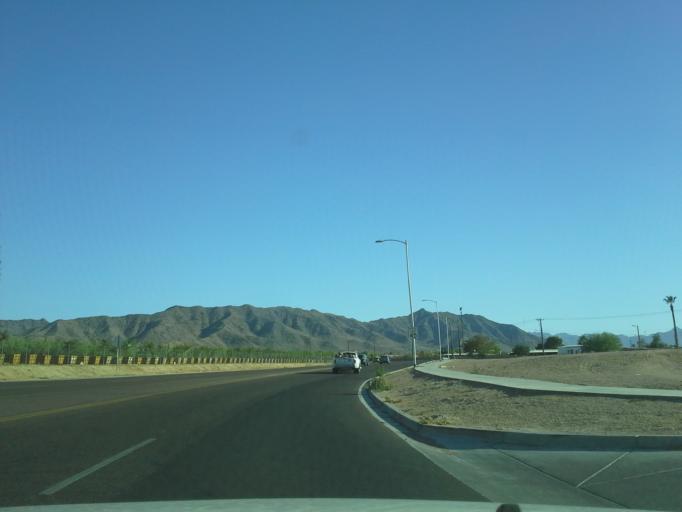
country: US
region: Arizona
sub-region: Maricopa County
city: Laveen
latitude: 33.3762
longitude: -112.0994
